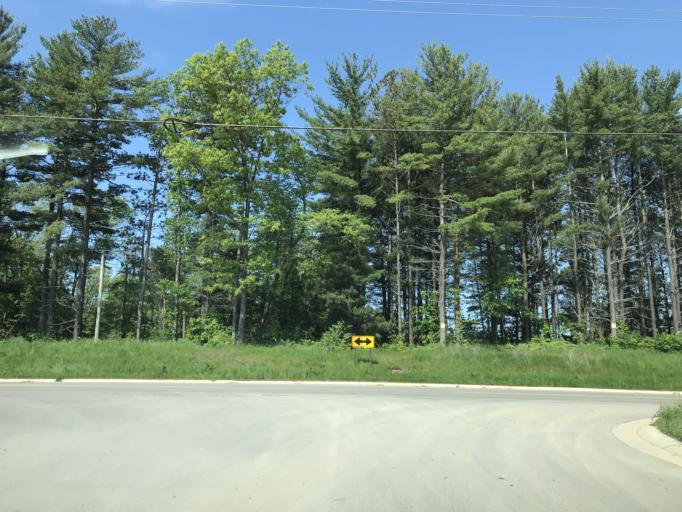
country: US
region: Michigan
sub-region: Oakland County
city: South Lyon
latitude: 42.4809
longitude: -83.6975
